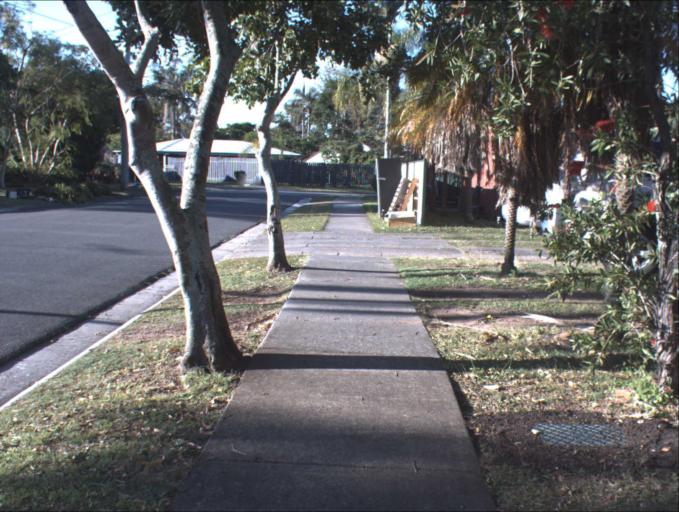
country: AU
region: Queensland
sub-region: Logan
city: Logan City
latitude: -27.6378
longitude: 153.1266
